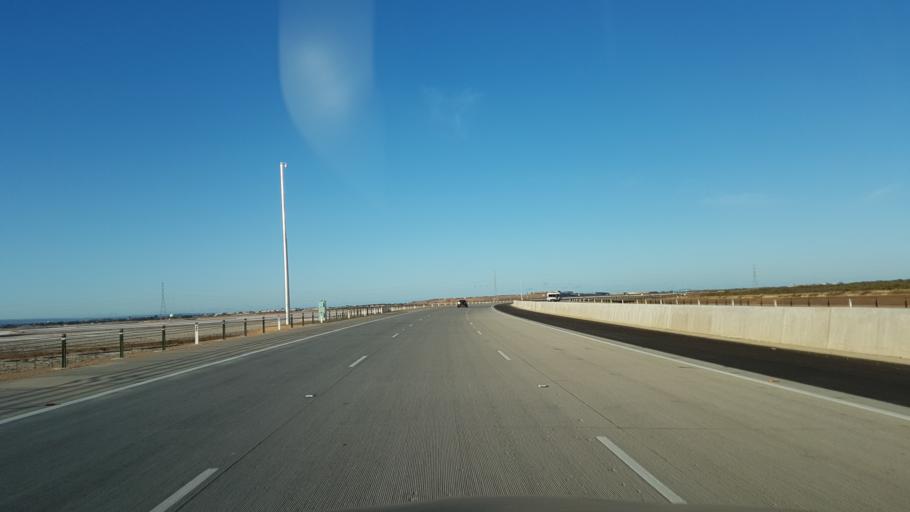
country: AU
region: South Australia
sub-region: Port Adelaide Enfield
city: Enfield
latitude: -34.8027
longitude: 138.5755
